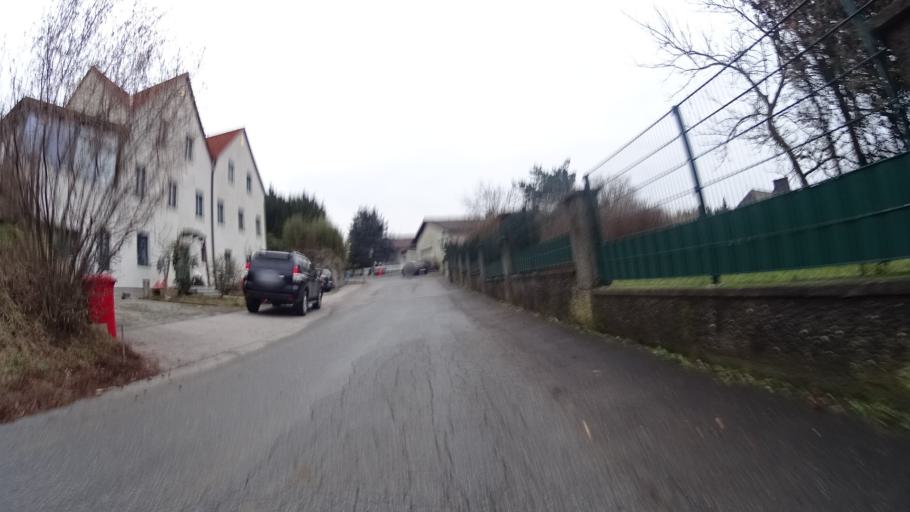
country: AT
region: Lower Austria
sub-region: Politischer Bezirk Korneuburg
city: Leobendorf
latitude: 48.3752
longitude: 16.3110
